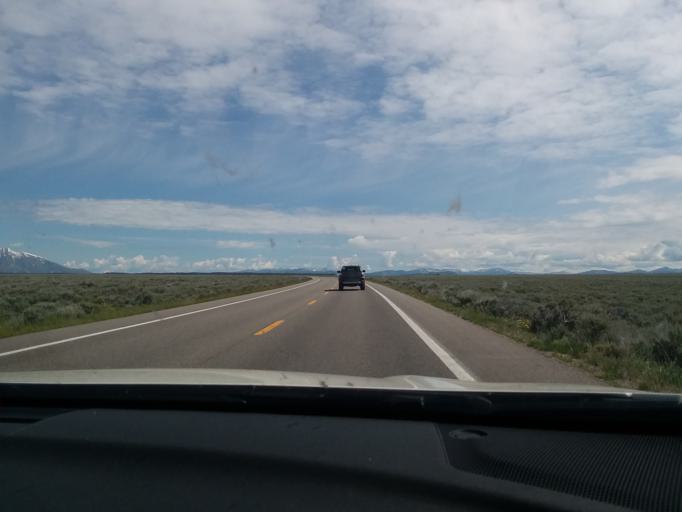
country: US
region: Wyoming
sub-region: Teton County
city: Jackson
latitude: 43.7030
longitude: -110.6660
